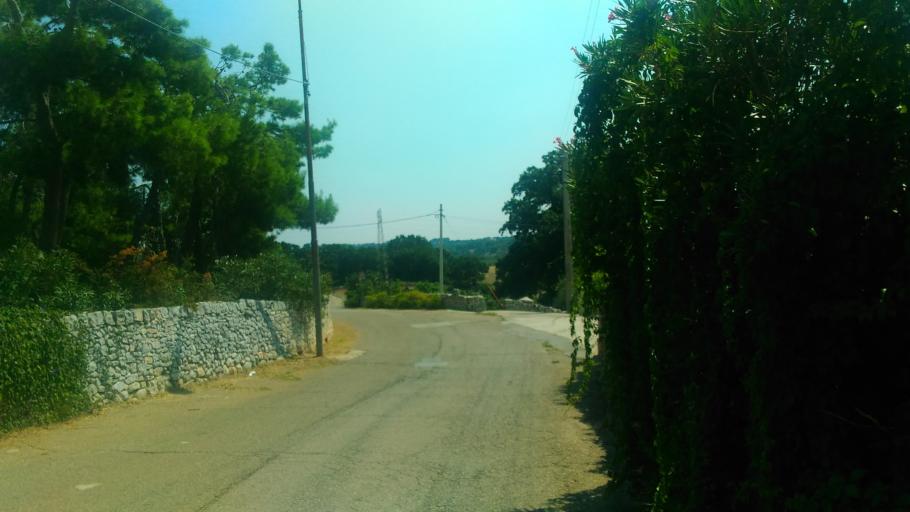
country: IT
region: Apulia
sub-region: Provincia di Brindisi
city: Cisternino
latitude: 40.7466
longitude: 17.3768
